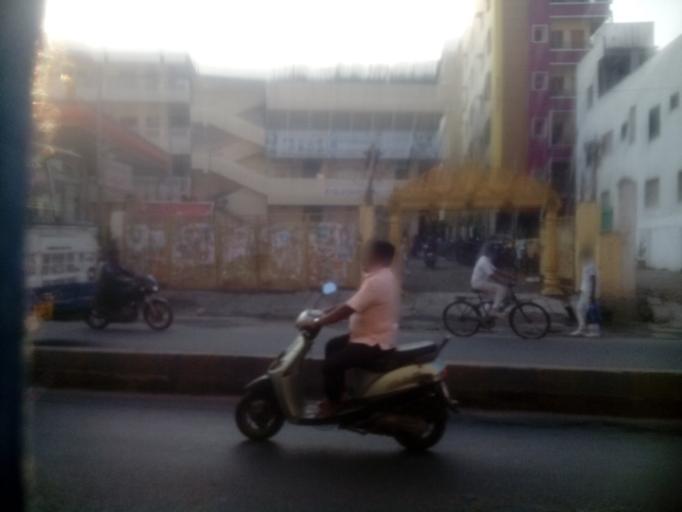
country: IN
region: Andhra Pradesh
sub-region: Krishna
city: Vijayawada
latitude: 16.5290
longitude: 80.6112
